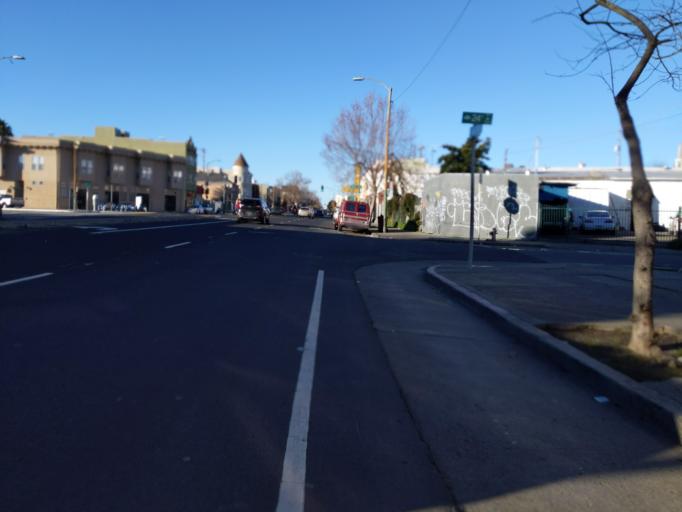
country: US
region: California
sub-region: Alameda County
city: Oakland
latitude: 37.8144
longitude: -122.2744
